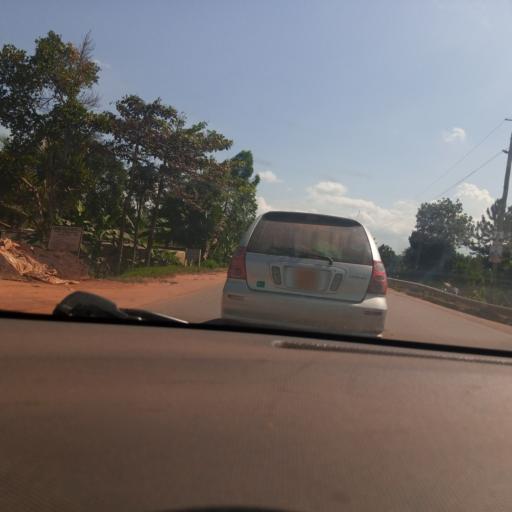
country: UG
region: Central Region
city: Masaka
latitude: -0.3137
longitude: 31.7453
